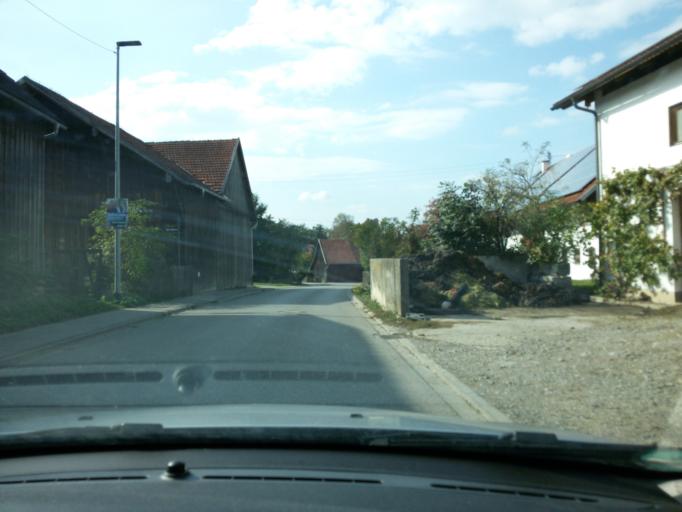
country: DE
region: Bavaria
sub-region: Swabia
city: Lamerdingen
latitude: 48.0851
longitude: 10.7699
